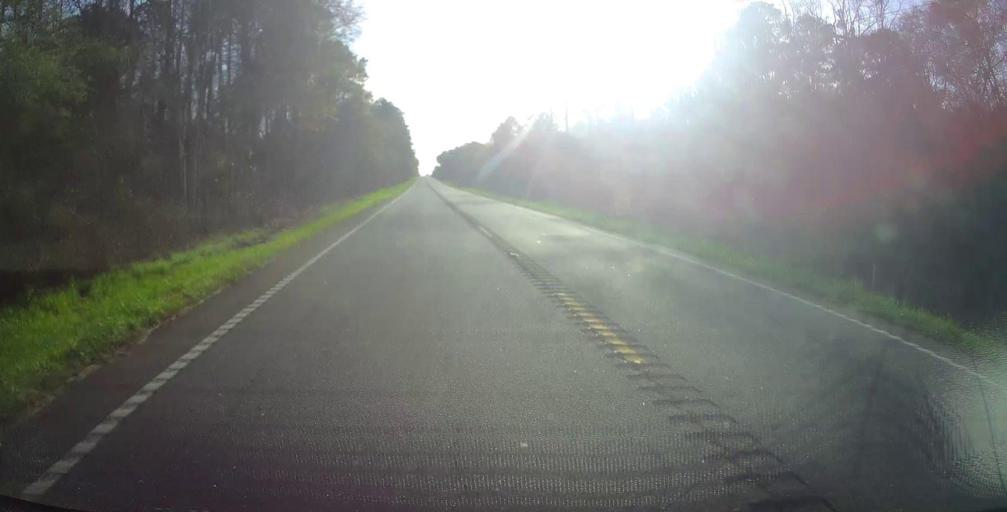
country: US
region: Georgia
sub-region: Tattnall County
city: Reidsville
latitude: 32.1260
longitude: -82.0584
